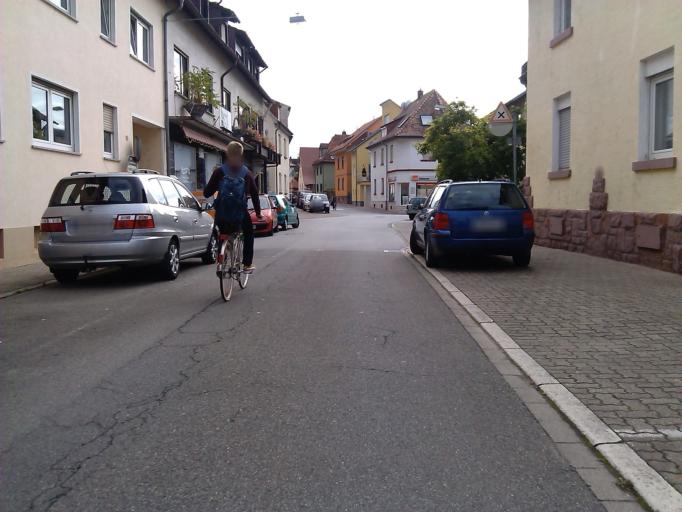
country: DE
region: Baden-Wuerttemberg
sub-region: Karlsruhe Region
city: Schriesheim
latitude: 49.4731
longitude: 8.6646
